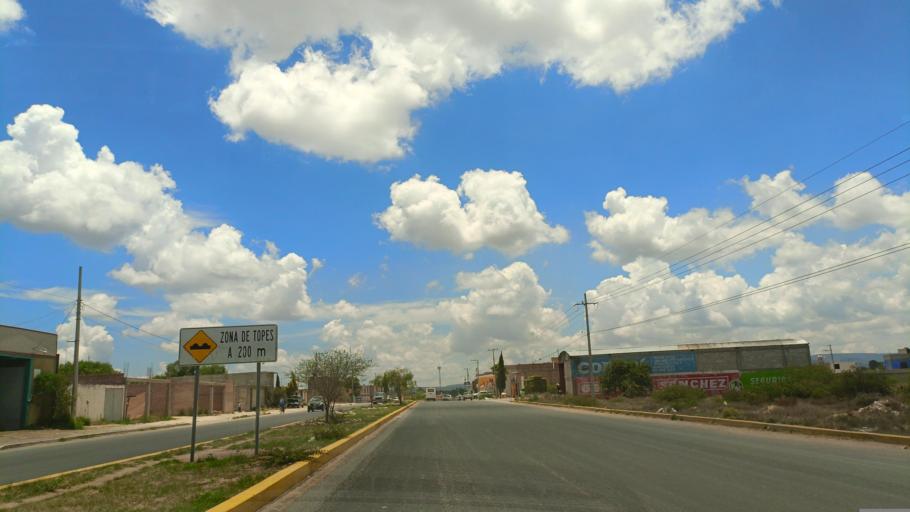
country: MX
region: Guanajuato
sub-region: San Luis de la Paz
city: San Luis de la Paz
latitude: 21.2897
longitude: -100.4987
